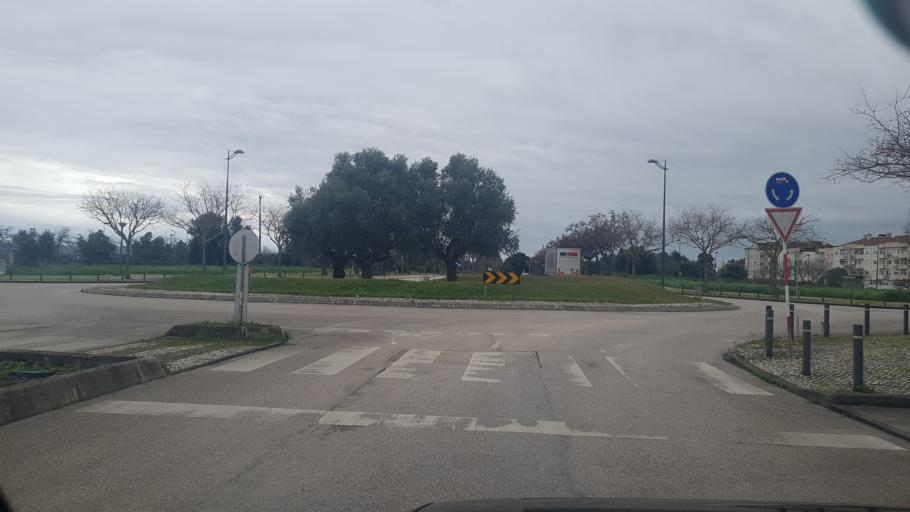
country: PT
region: Santarem
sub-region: Entroncamento
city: Entroncamento
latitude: 39.4594
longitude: -8.4649
